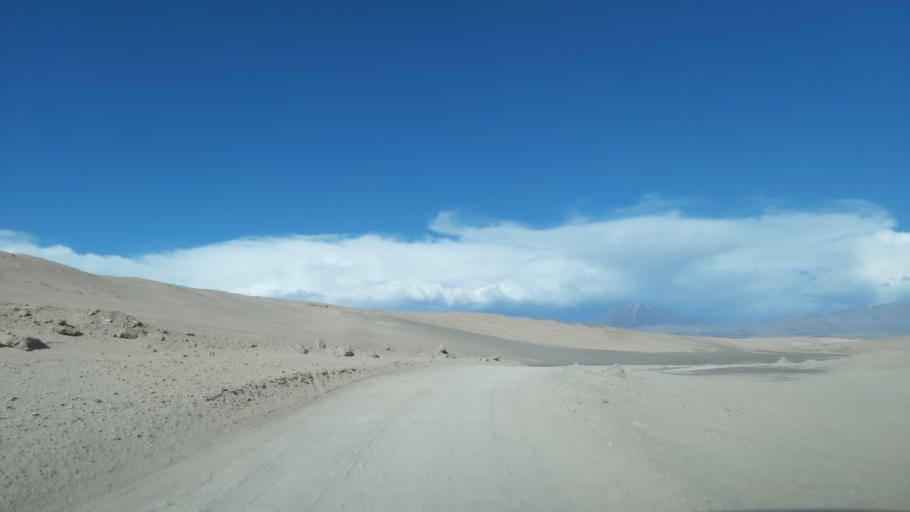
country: CL
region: Atacama
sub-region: Provincia de Chanaral
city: Diego de Almagro
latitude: -26.2710
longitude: -69.0958
